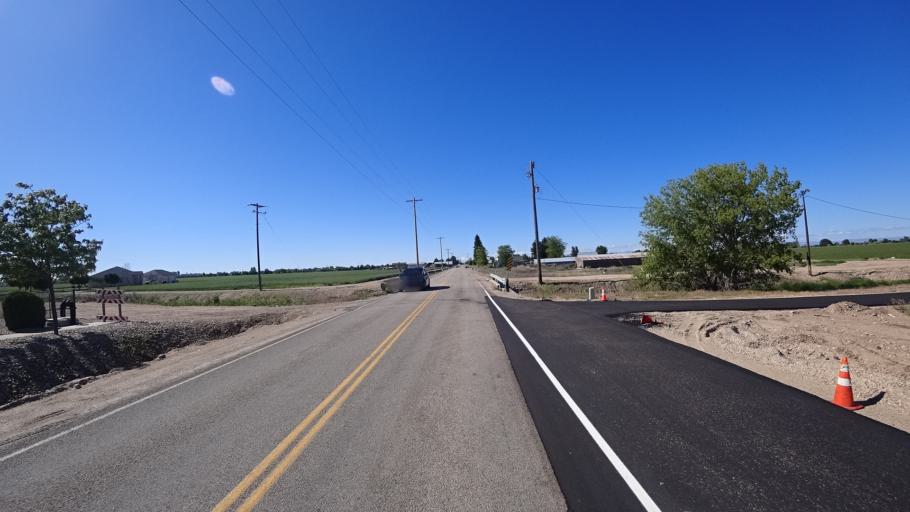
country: US
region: Idaho
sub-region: Ada County
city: Star
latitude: 43.6429
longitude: -116.4536
